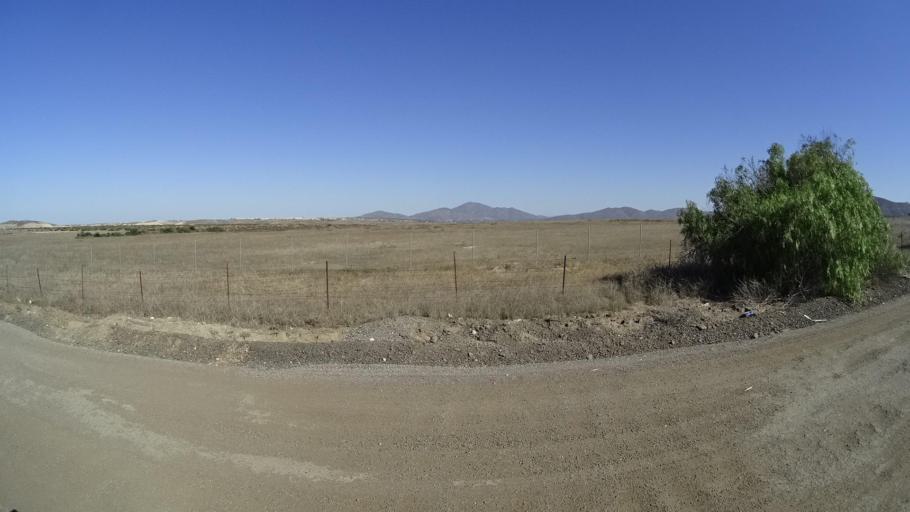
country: MX
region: Baja California
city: Tijuana
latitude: 32.5785
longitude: -116.9495
